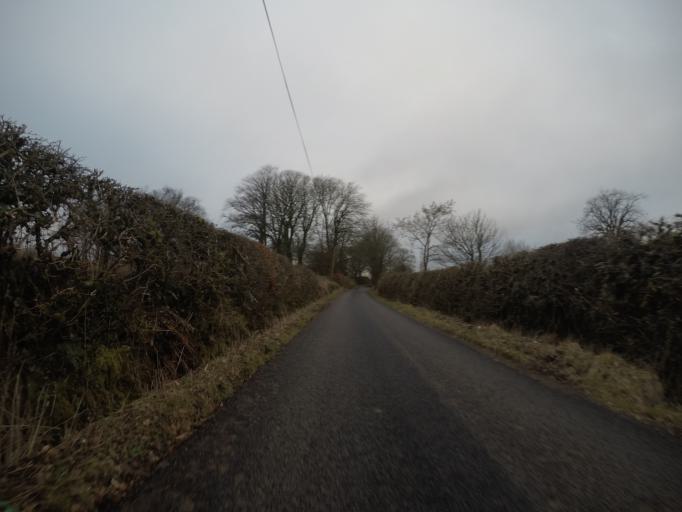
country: GB
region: Scotland
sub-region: North Ayrshire
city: Dalry
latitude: 55.7146
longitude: -4.7557
